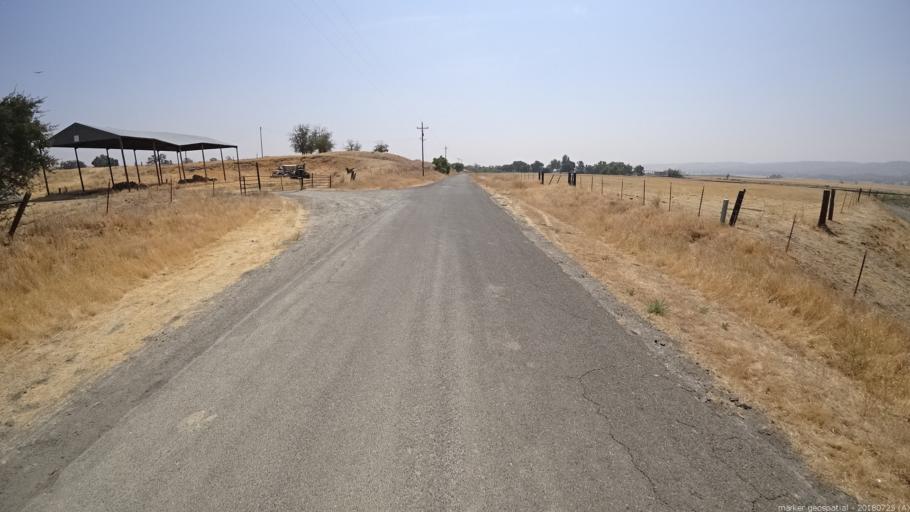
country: US
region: California
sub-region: San Luis Obispo County
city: Shandon
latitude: 35.8492
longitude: -120.3819
